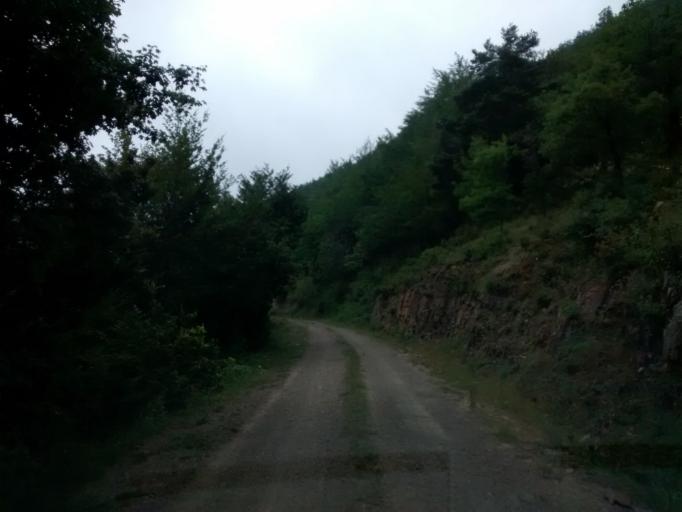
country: ES
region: La Rioja
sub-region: Provincia de La Rioja
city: Ajamil
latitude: 42.1365
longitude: -2.4815
